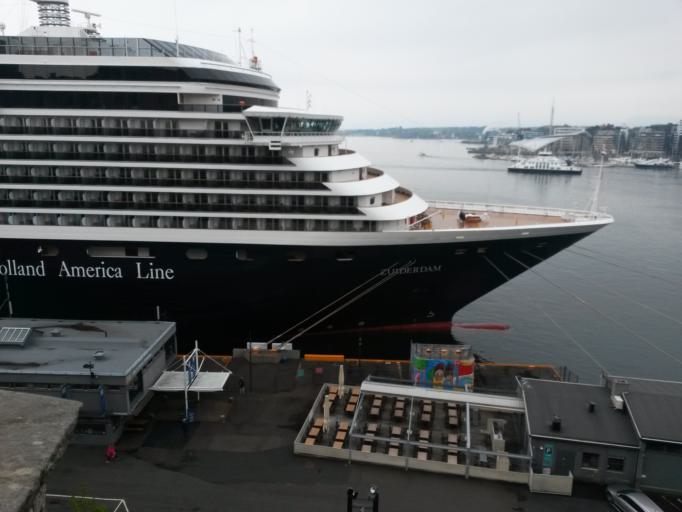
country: NO
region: Oslo
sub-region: Oslo
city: Oslo
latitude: 59.9072
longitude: 10.7356
